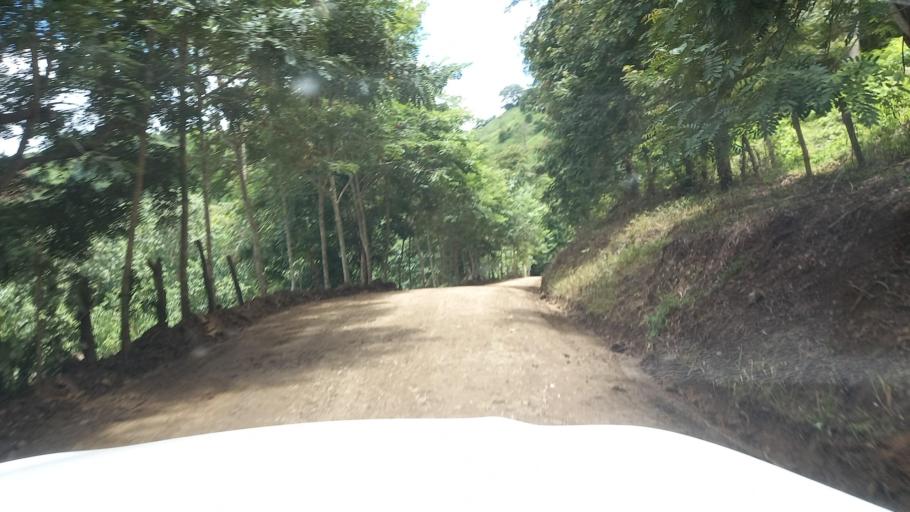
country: NI
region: Nueva Segovia
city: Wiwili
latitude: 13.7232
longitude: -85.7849
